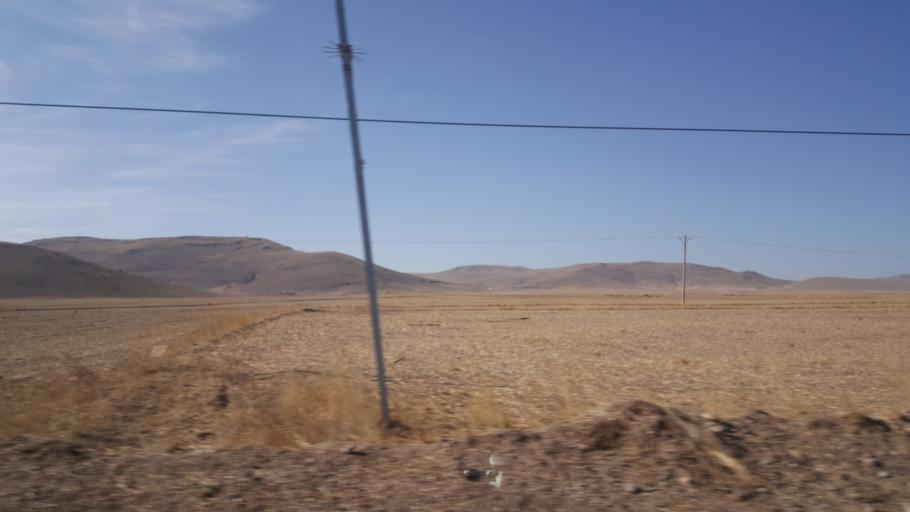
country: TR
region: Ankara
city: Altpinar
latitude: 39.1872
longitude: 32.7394
